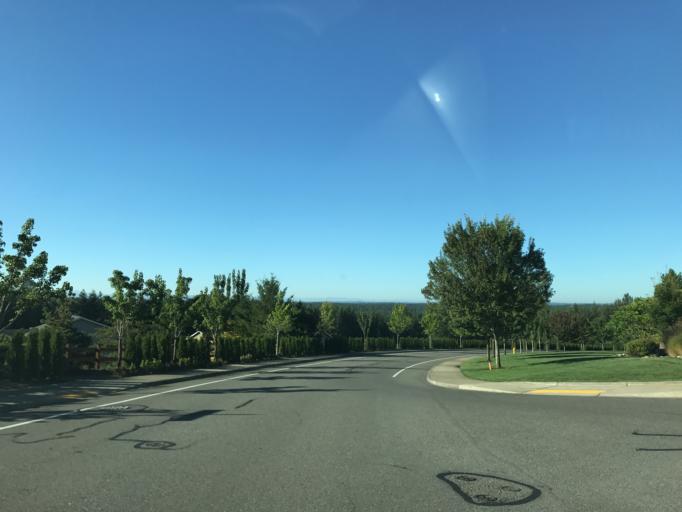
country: US
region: Washington
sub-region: King County
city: Ravensdale
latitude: 47.3527
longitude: -122.0008
